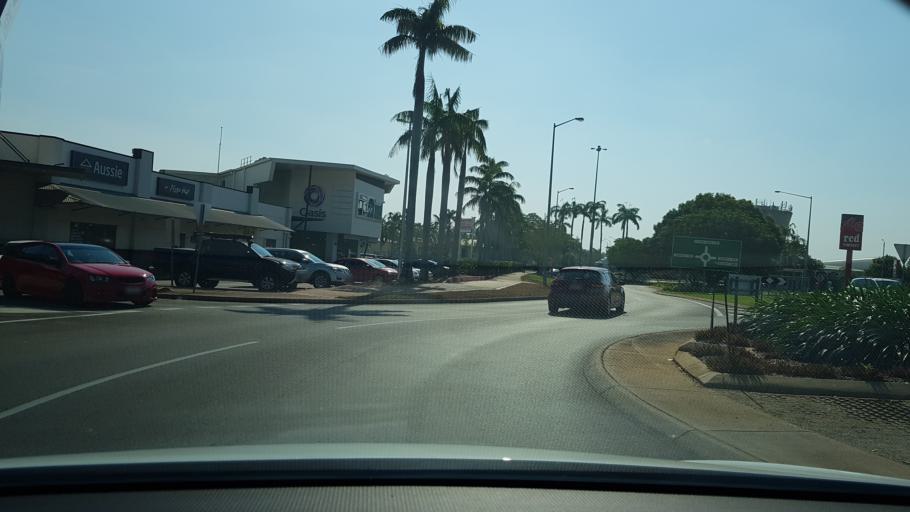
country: AU
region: Northern Territory
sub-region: Palmerston
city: Palmerston
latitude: -12.4834
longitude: 130.9865
